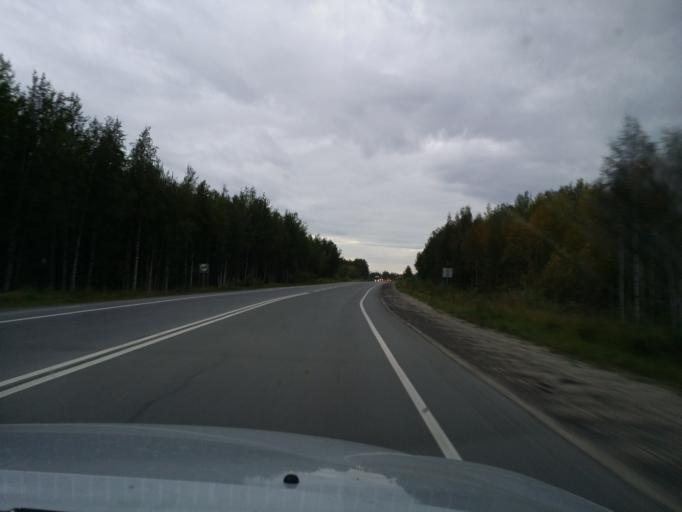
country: RU
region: Khanty-Mansiyskiy Avtonomnyy Okrug
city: Izluchinsk
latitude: 61.0299
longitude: 76.8806
